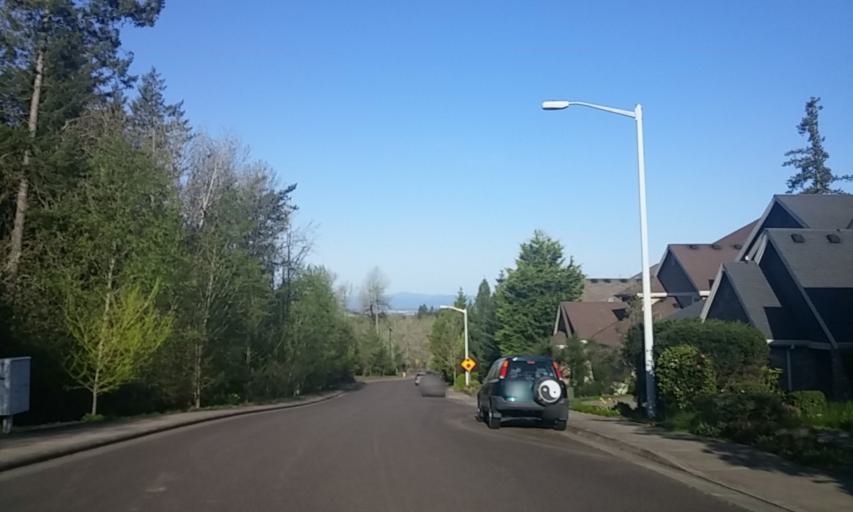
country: US
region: Oregon
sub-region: Washington County
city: Cedar Mill
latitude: 45.5444
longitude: -122.7915
